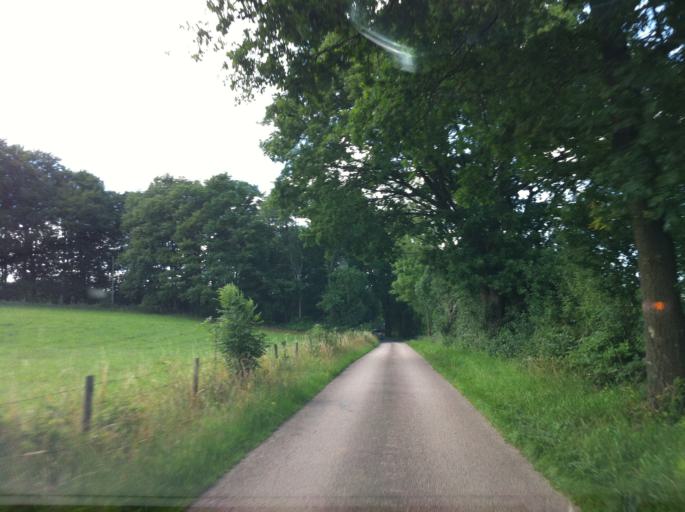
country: SE
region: Skane
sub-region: Astorps Kommun
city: Kvidinge
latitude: 56.1036
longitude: 13.0817
